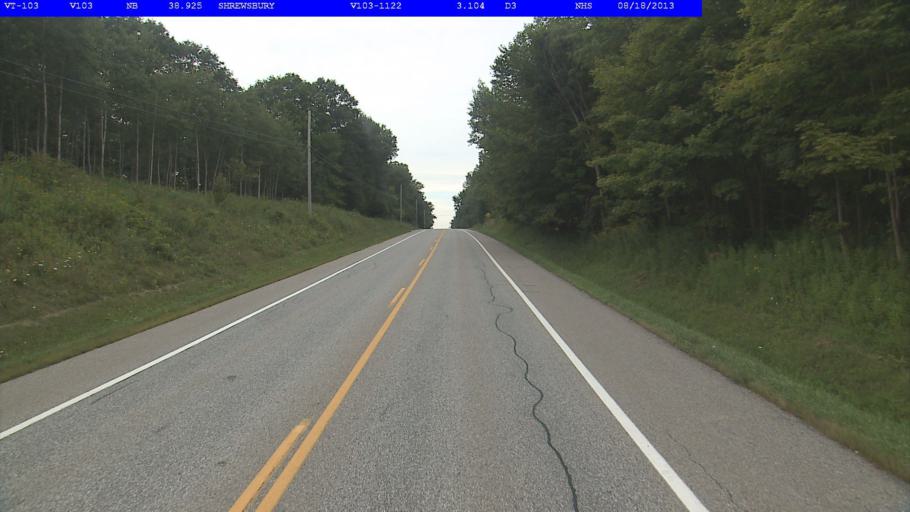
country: US
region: Vermont
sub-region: Rutland County
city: Rutland
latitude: 43.5132
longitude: -72.9147
